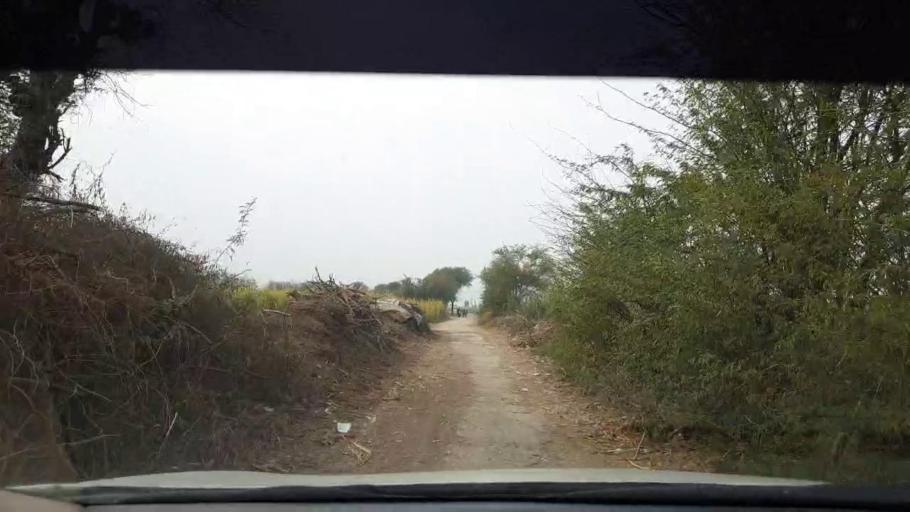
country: PK
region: Sindh
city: Berani
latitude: 25.8645
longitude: 68.7954
